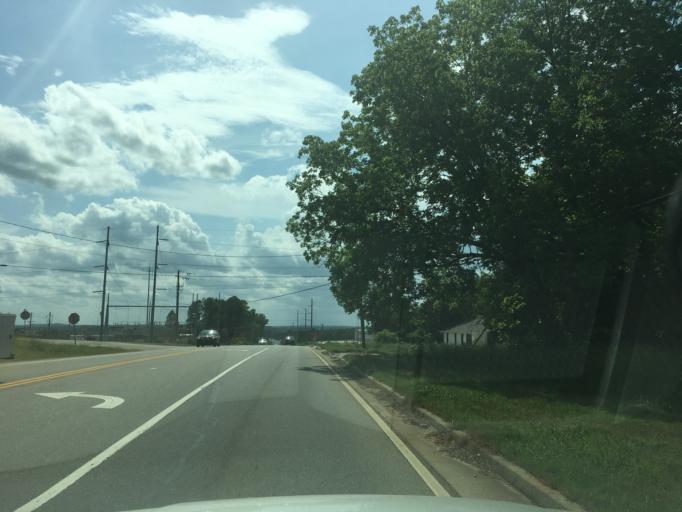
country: US
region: Georgia
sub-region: Jackson County
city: Braselton
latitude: 34.1073
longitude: -83.7680
